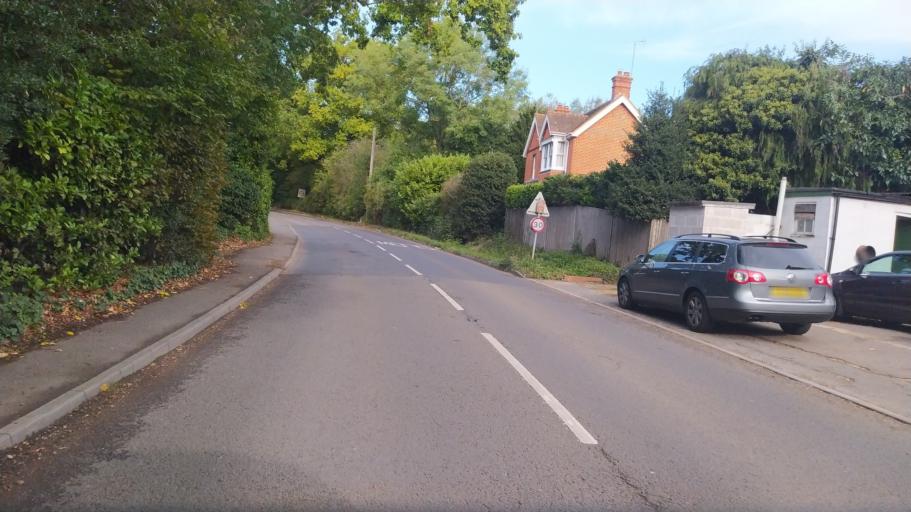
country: GB
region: England
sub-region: Hampshire
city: Eversley
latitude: 51.3575
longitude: -0.8887
